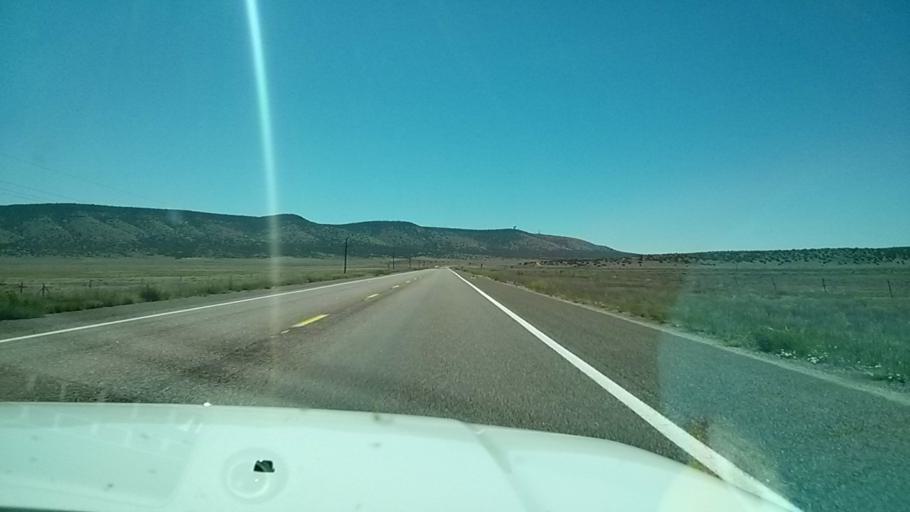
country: US
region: Arizona
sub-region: Mohave County
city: Peach Springs
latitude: 35.3884
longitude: -112.9969
